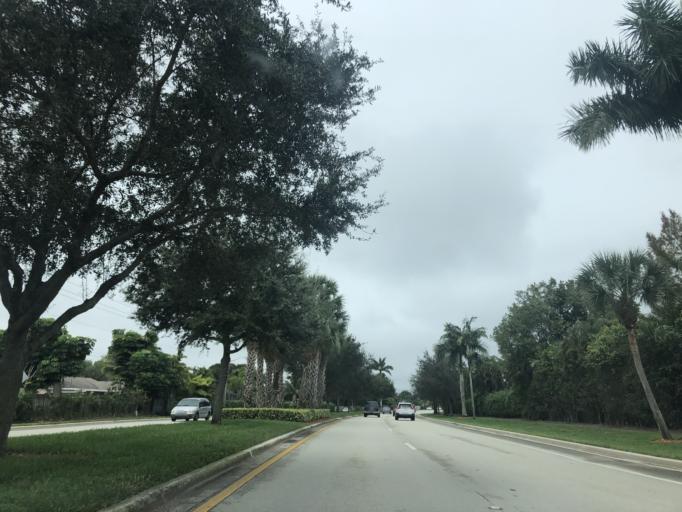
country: US
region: Florida
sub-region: Palm Beach County
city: Wellington
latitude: 26.6635
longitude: -80.2436
